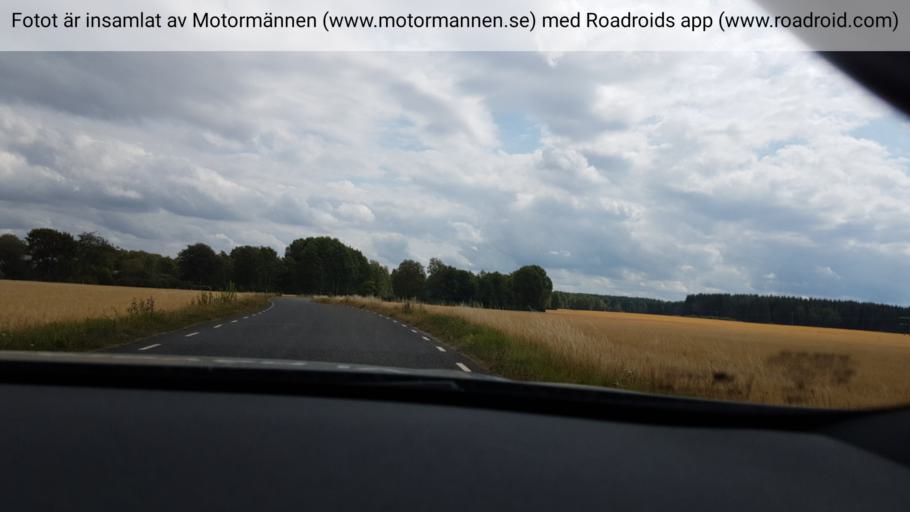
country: SE
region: Vaestra Goetaland
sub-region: Falkopings Kommun
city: Floby
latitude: 58.1275
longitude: 13.3640
